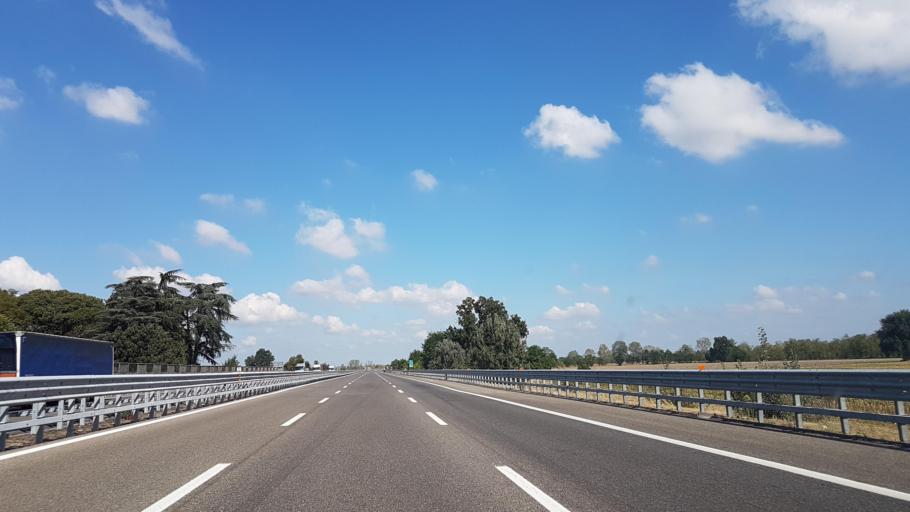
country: IT
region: Piedmont
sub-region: Provincia di Alessandria
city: Castelnuovo Scrivia
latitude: 44.9428
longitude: 8.8584
